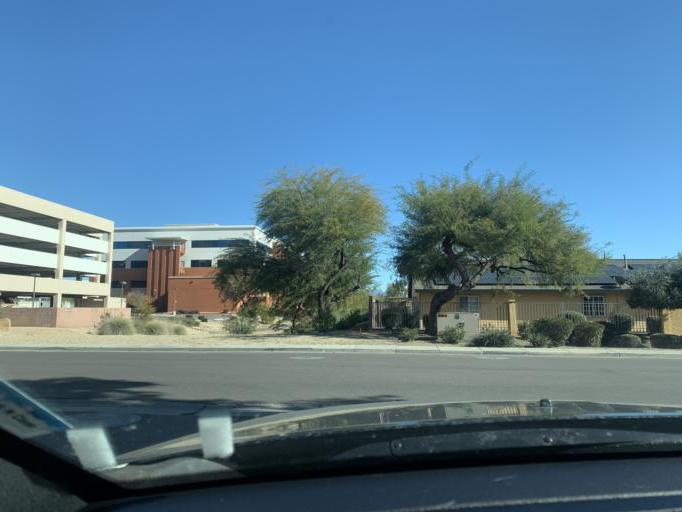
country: US
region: Arizona
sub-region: Maricopa County
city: Paradise Valley
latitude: 33.6381
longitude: -112.0006
